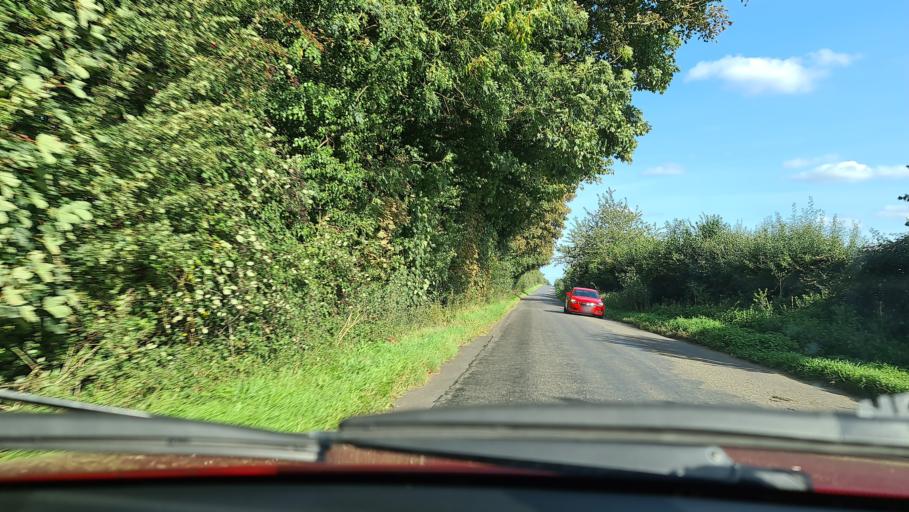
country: GB
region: England
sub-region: Oxfordshire
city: Adderbury
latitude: 52.0231
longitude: -1.2486
